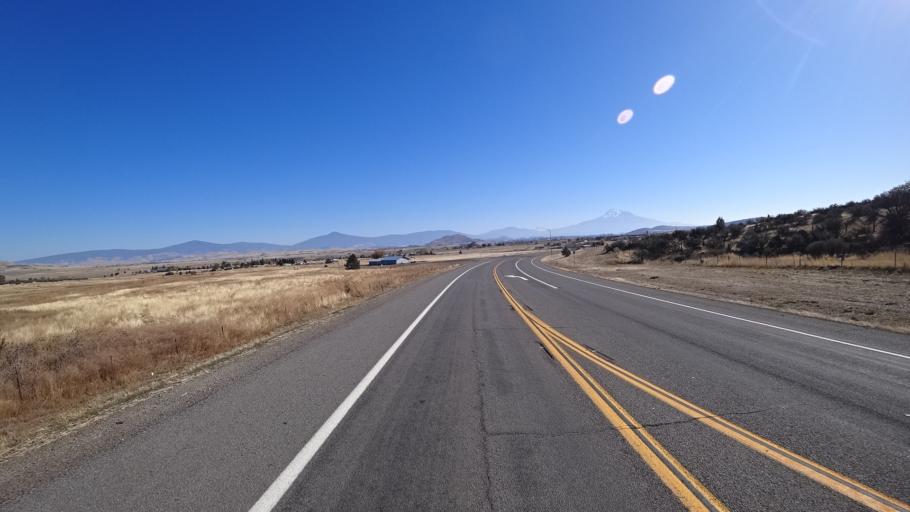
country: US
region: California
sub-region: Siskiyou County
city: Yreka
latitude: 41.7418
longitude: -122.6002
